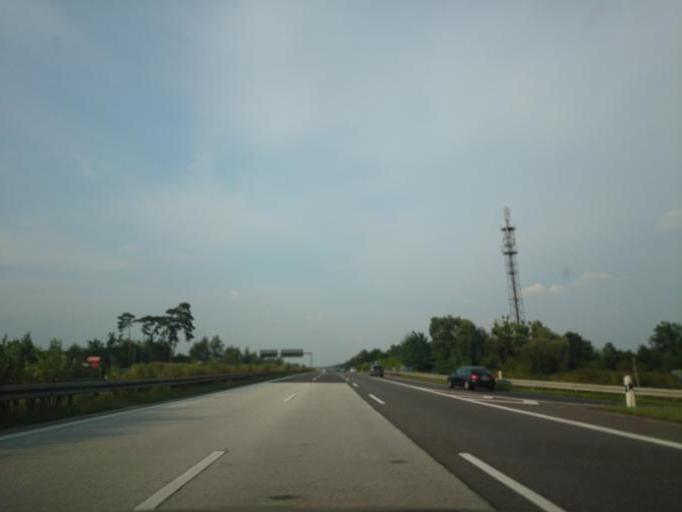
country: DE
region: Brandenburg
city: Stahnsdorf
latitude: 52.4016
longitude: 13.1866
